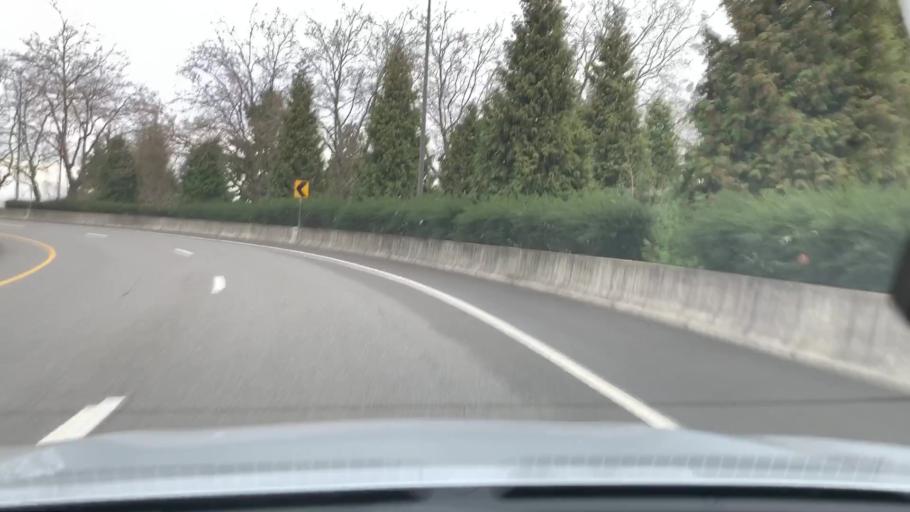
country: US
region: Washington
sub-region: King County
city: SeaTac
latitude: 47.4585
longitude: -122.2979
